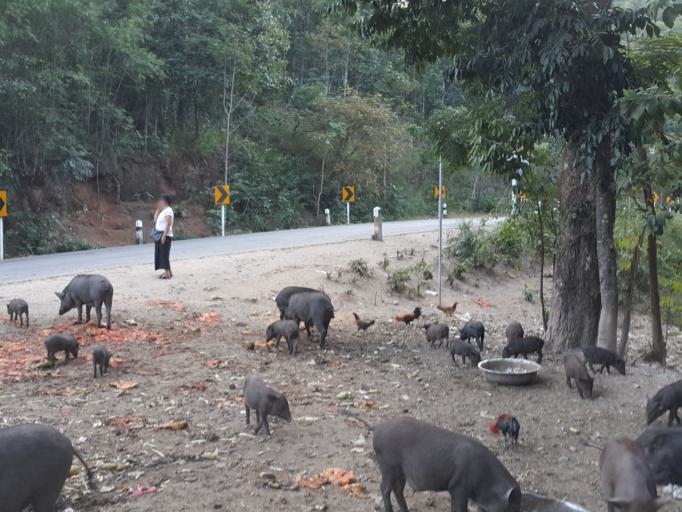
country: TH
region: Lampang
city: Thoen
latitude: 17.6218
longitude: 99.3144
